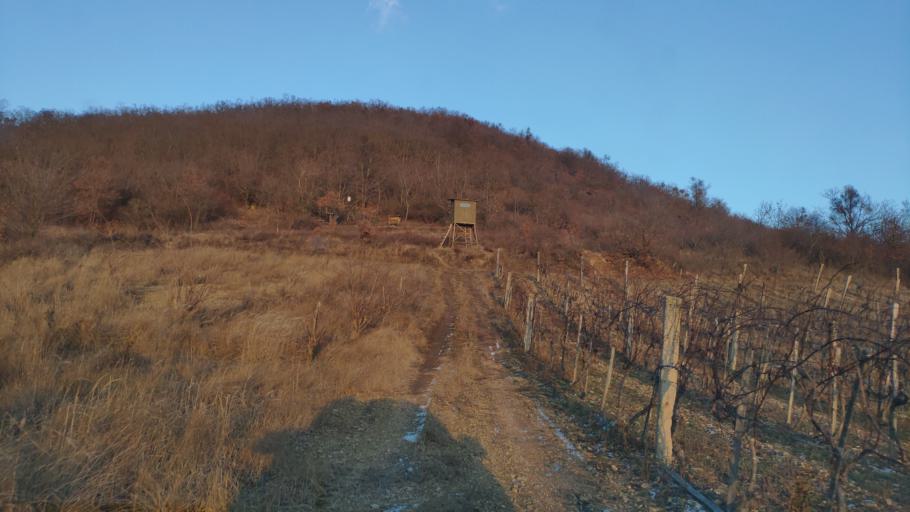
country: HU
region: Borsod-Abauj-Zemplen
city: Olaszliszka
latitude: 48.2779
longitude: 21.3992
